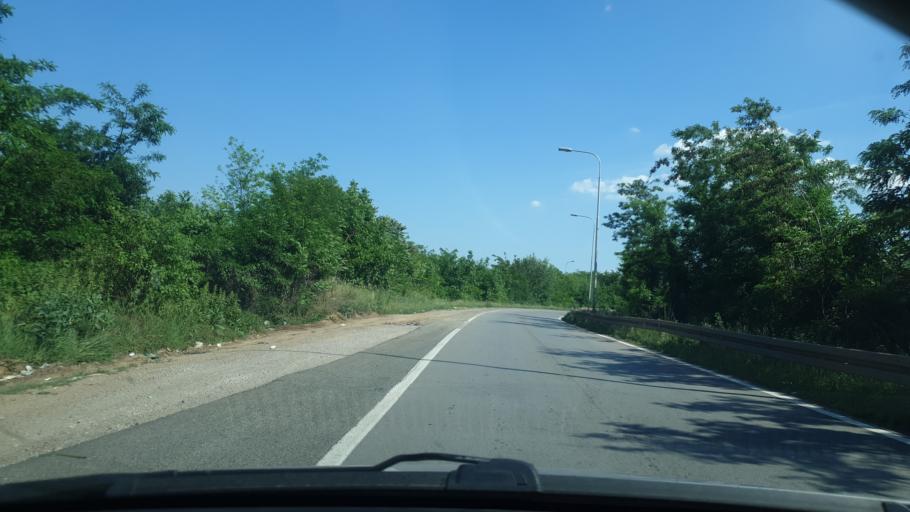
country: RS
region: Central Serbia
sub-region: Podunavski Okrug
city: Smederevo
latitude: 44.6084
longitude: 20.9542
